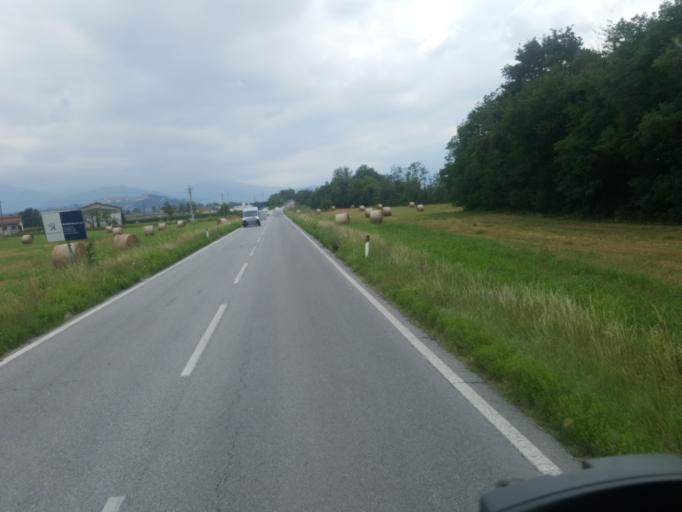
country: IT
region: Piedmont
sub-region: Provincia di Cuneo
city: Bastia Mondovi
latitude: 44.4301
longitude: 7.8596
